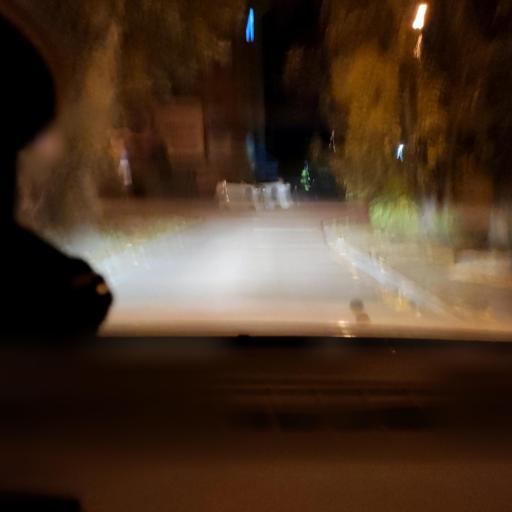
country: RU
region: Samara
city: Samara
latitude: 53.2429
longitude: 50.2407
